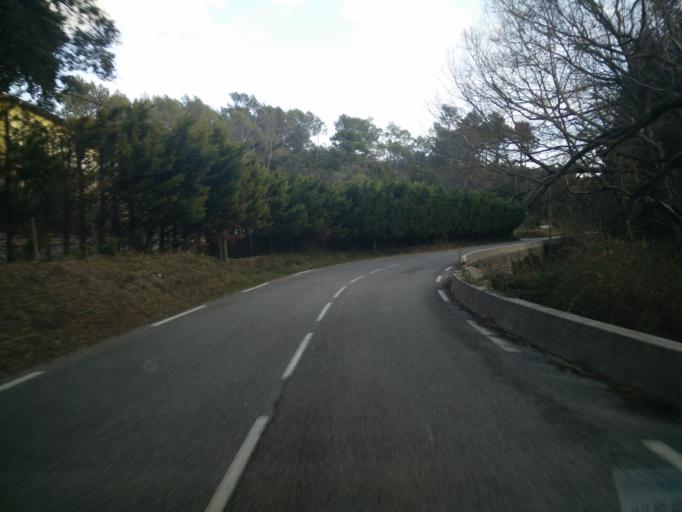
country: FR
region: Provence-Alpes-Cote d'Azur
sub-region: Departement du Var
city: Signes
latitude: 43.2831
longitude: 5.8980
